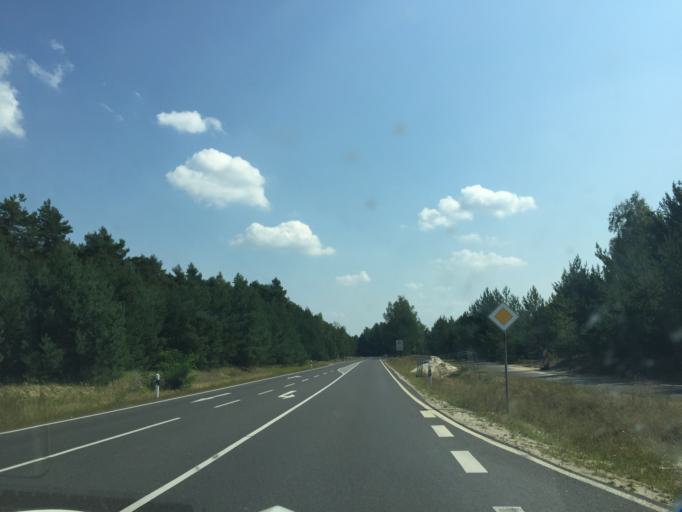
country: DE
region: Saxony
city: Uhyst
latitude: 51.4003
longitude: 14.5183
